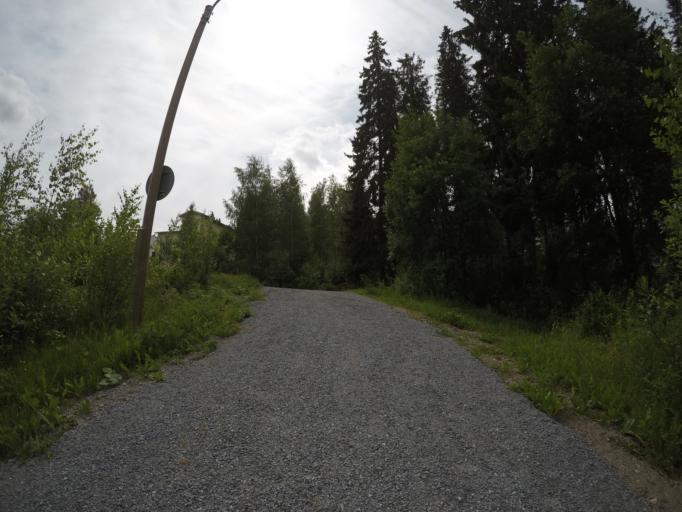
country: FI
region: Haeme
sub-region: Haemeenlinna
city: Haemeenlinna
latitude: 60.9835
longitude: 24.4768
